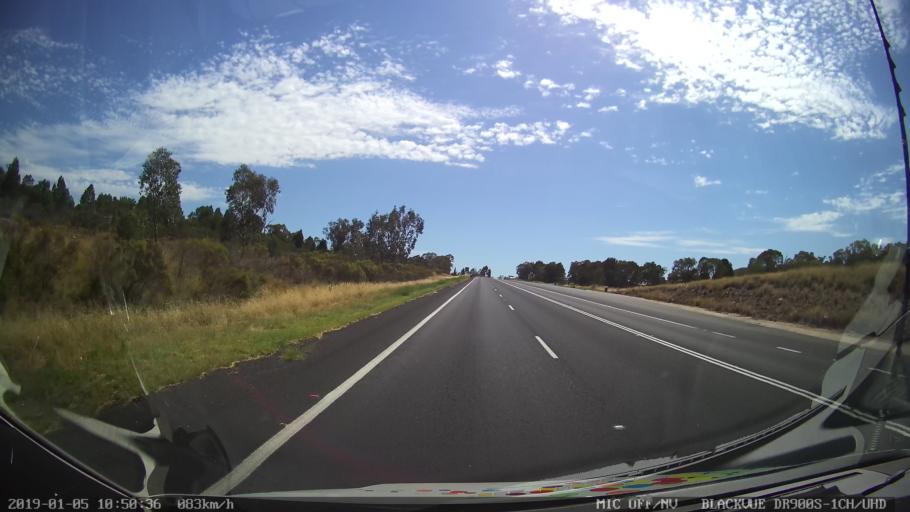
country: AU
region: New South Wales
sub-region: Warrumbungle Shire
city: Coonabarabran
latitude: -31.4280
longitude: 149.0776
